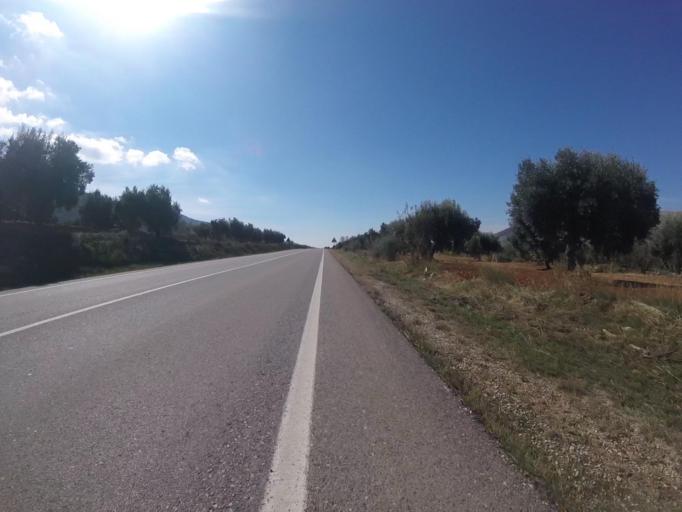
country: ES
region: Valencia
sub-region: Provincia de Castello
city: Sierra-Engarceran
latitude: 40.3179
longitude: -0.0289
